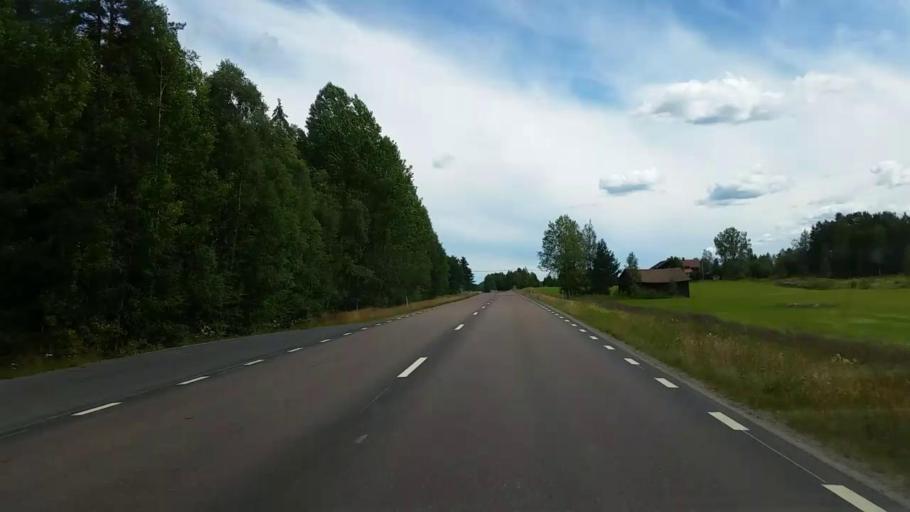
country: SE
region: Gaevleborg
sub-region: Ovanakers Kommun
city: Edsbyn
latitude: 61.3680
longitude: 15.8672
